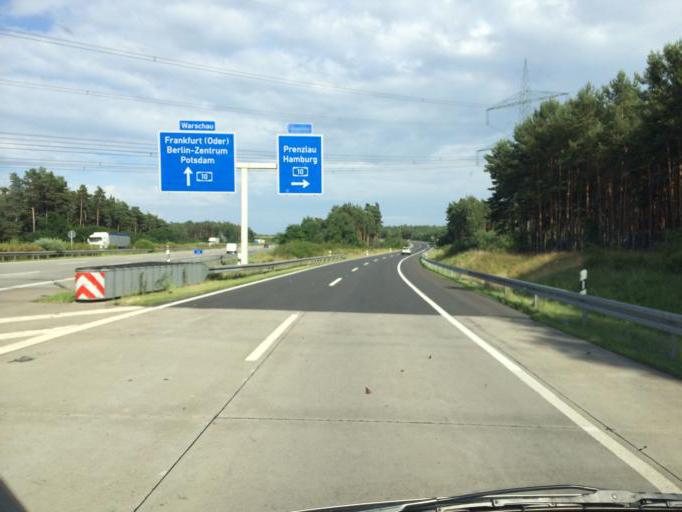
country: DE
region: Brandenburg
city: Gross Kreutz
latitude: 52.3380
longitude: 12.8017
